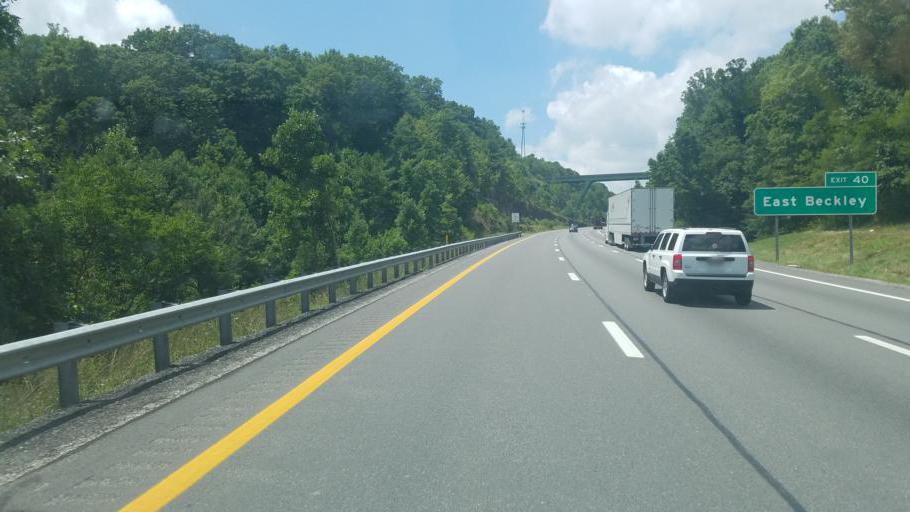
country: US
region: West Virginia
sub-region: Raleigh County
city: Beaver
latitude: 37.7226
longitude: -81.1780
